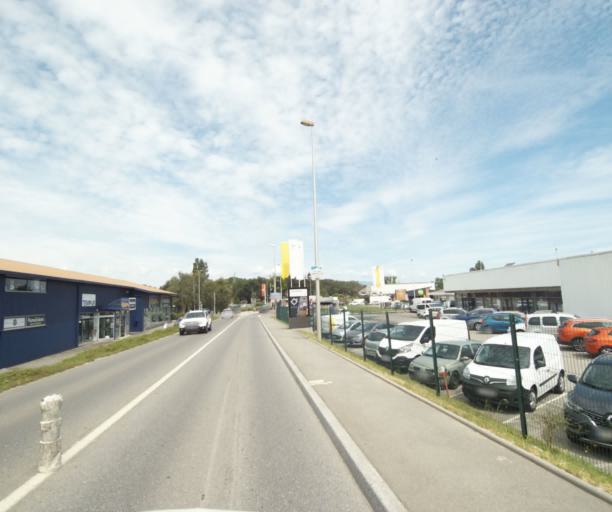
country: FR
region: Rhone-Alpes
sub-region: Departement de la Haute-Savoie
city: Anthy-sur-Leman
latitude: 46.3514
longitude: 6.4404
